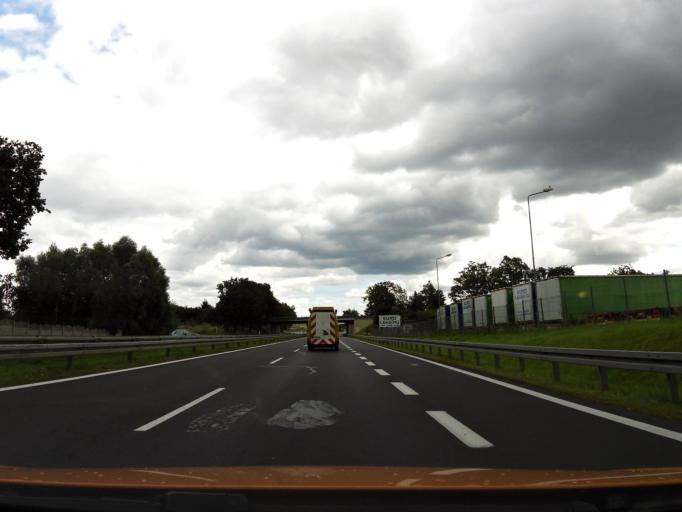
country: PL
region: West Pomeranian Voivodeship
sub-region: Powiat policki
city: Kolbaskowo
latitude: 53.3401
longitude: 14.4408
